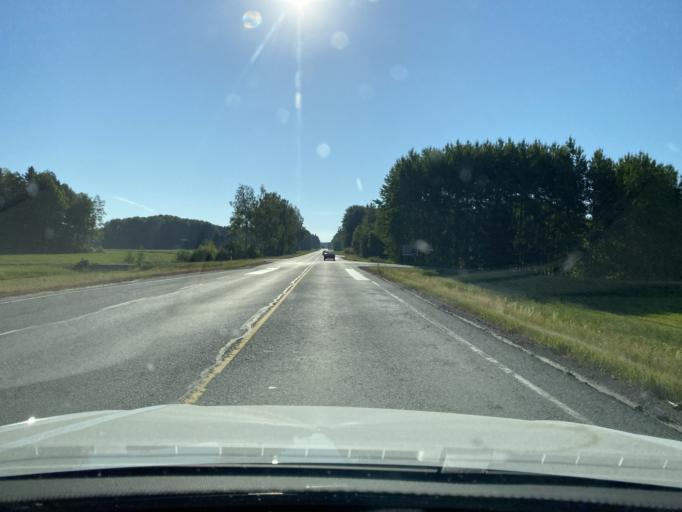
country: FI
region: Haeme
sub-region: Forssa
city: Tammela
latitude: 60.8259
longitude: 23.7646
